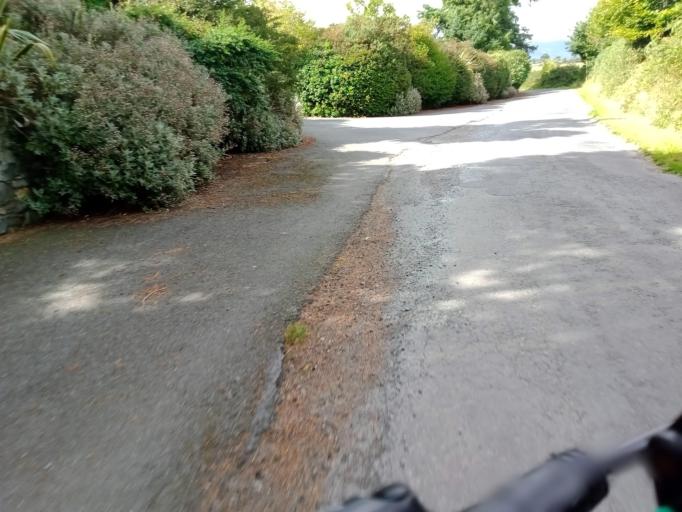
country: IE
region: Munster
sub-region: Waterford
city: Dungarvan
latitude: 52.1372
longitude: -7.4770
